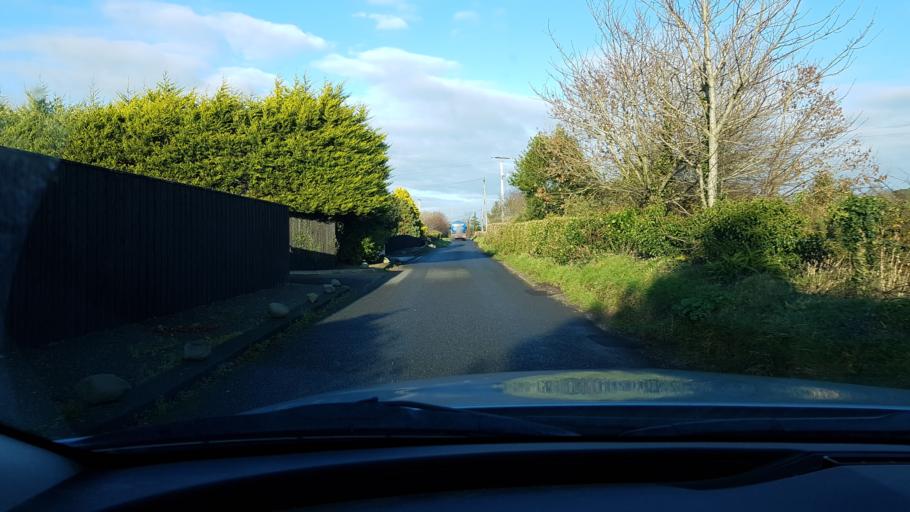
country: GB
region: Northern Ireland
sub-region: Ards District
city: Greyabbey
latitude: 54.5558
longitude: -5.5474
